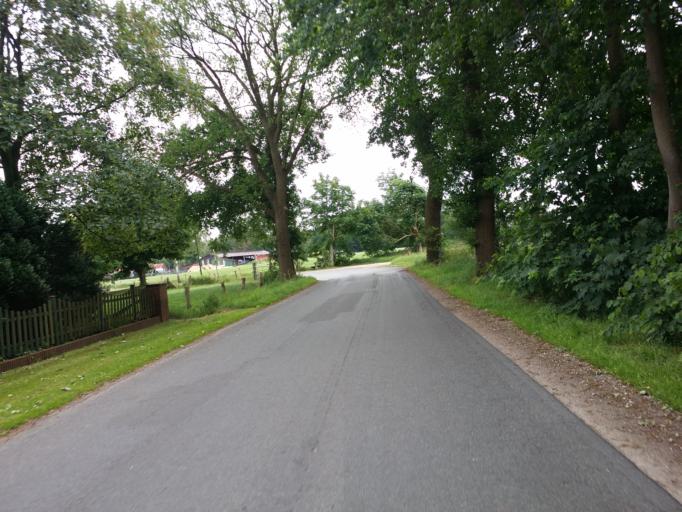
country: DE
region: Lower Saxony
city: Wiefelstede
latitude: 53.3054
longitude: 8.0545
